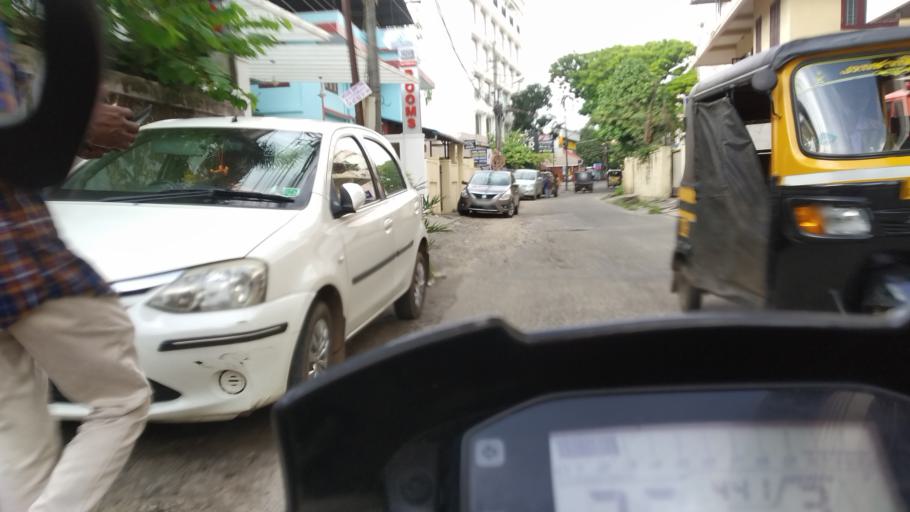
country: IN
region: Kerala
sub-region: Ernakulam
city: Cochin
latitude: 9.9914
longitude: 76.2849
